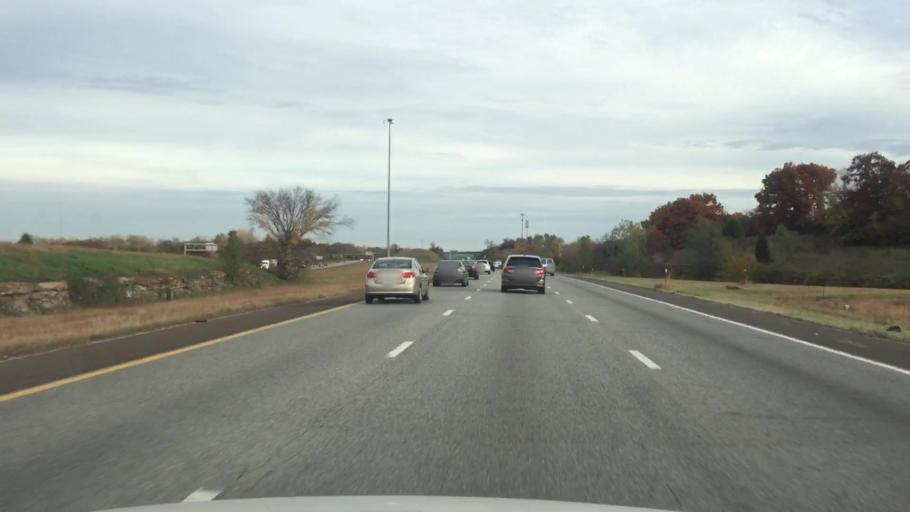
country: US
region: Kansas
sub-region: Wyandotte County
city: Edwardsville
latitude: 39.0242
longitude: -94.7856
